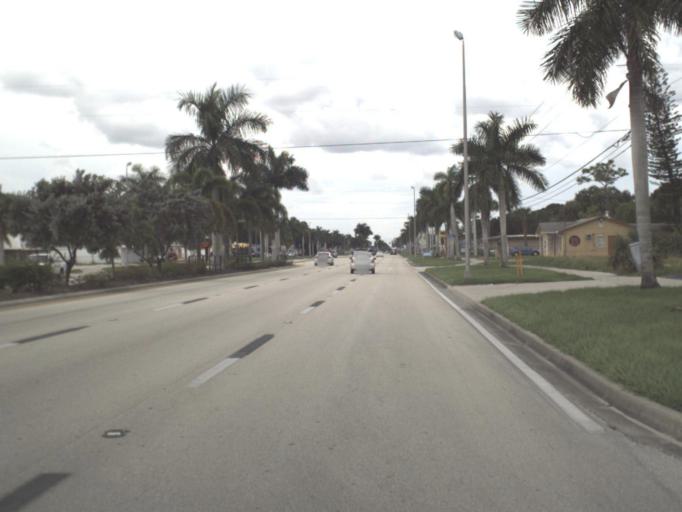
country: US
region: Florida
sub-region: Lee County
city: Tice
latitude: 26.6778
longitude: -81.8101
